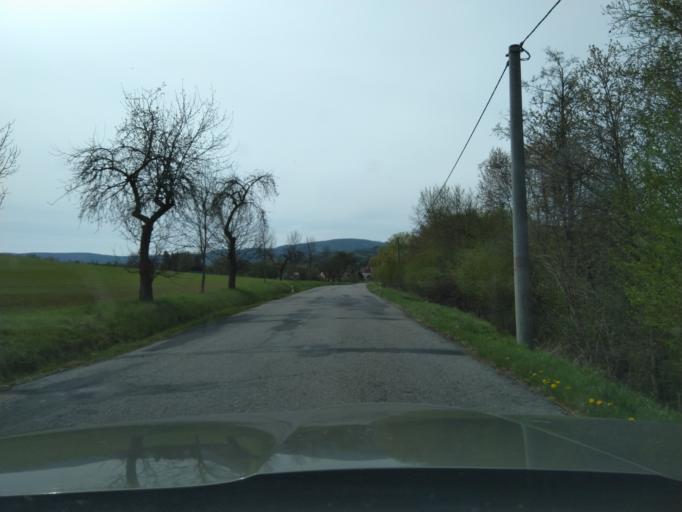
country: CZ
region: Plzensky
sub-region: Okres Klatovy
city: Kasperske Hory
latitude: 49.2101
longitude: 13.6127
